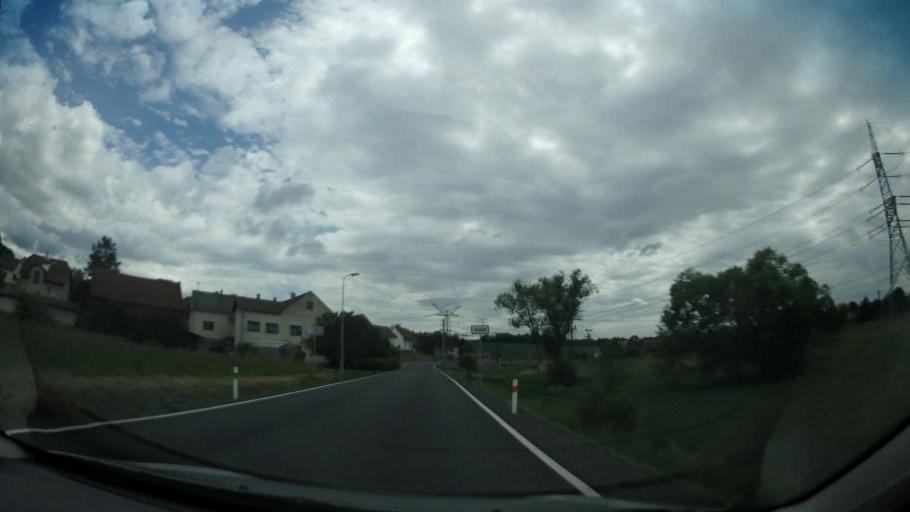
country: CZ
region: Pardubicky
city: Kuncina
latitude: 49.8487
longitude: 16.6961
